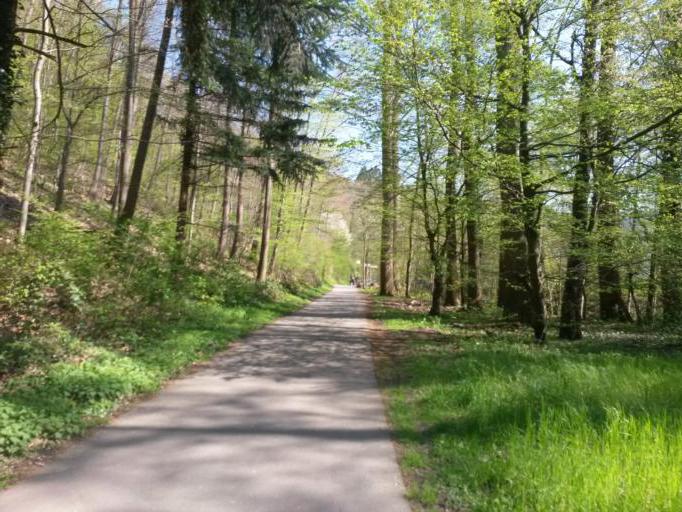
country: DE
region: Baden-Wuerttemberg
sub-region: Karlsruhe Region
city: Konigsbach-Stein
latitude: 48.9691
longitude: 8.5564
